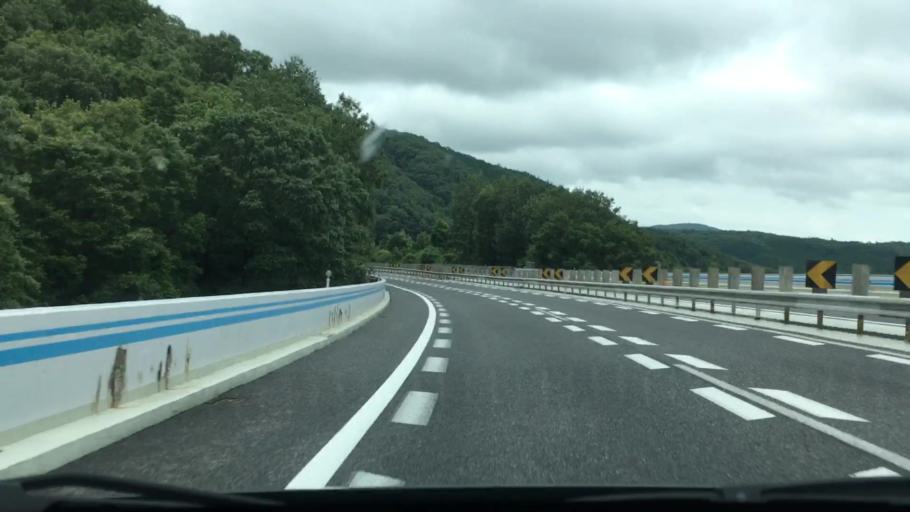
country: JP
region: Hiroshima
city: Miyoshi
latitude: 34.7834
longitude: 132.8444
